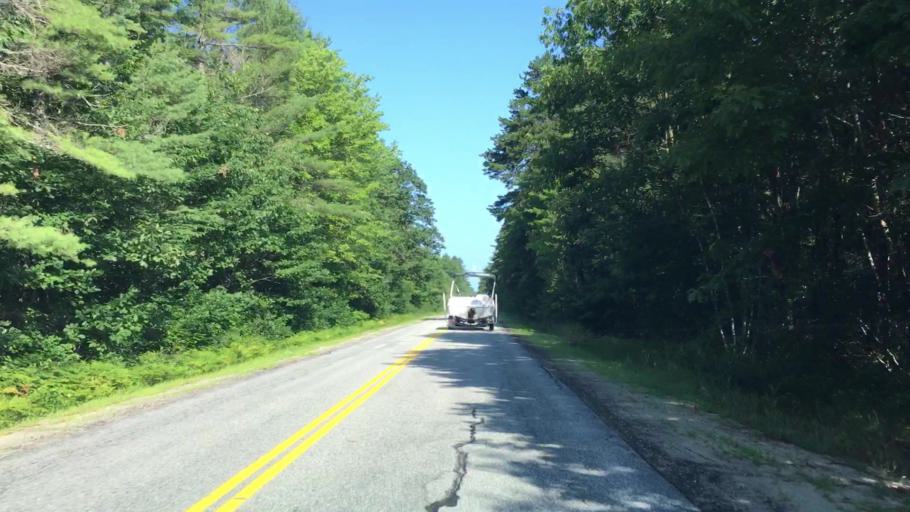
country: US
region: Maine
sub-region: Androscoggin County
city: Poland
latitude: 44.0469
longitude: -70.3621
